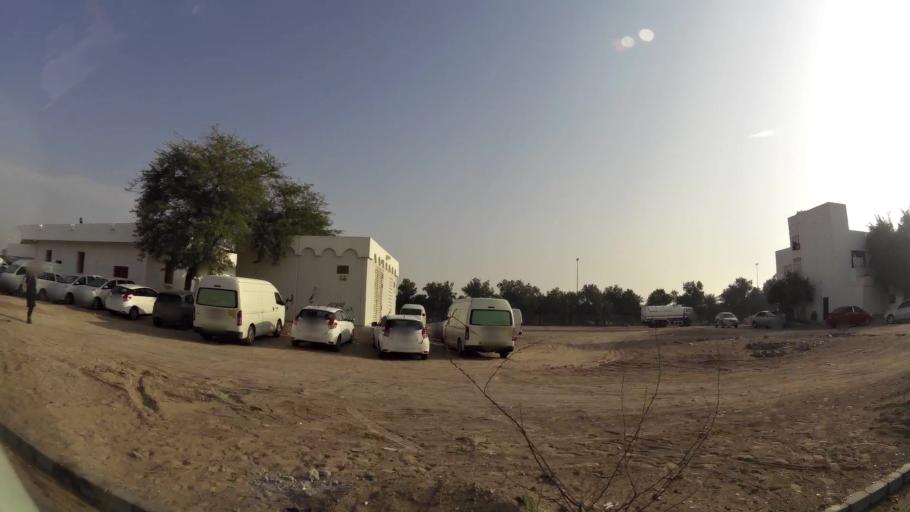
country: AE
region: Abu Dhabi
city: Abu Dhabi
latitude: 24.2971
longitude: 54.6245
